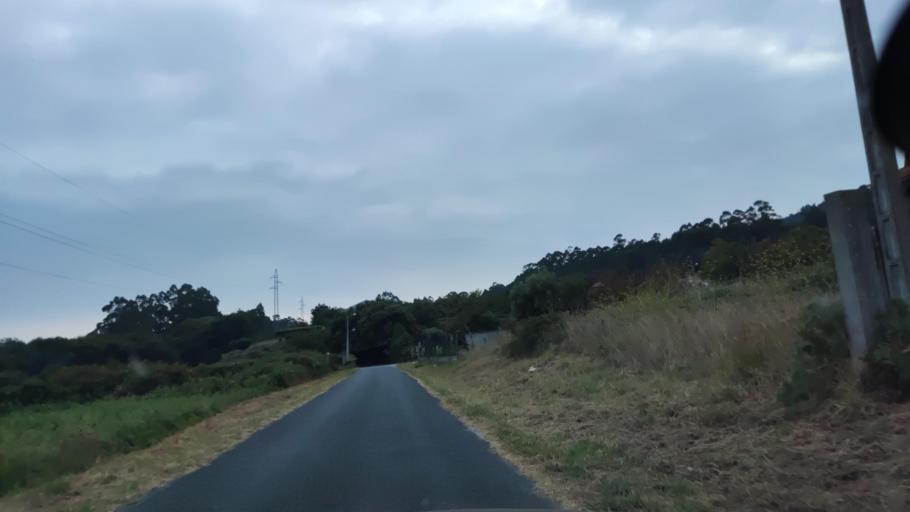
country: ES
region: Galicia
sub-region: Provincia de Pontevedra
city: Catoira
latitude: 42.7098
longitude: -8.7214
